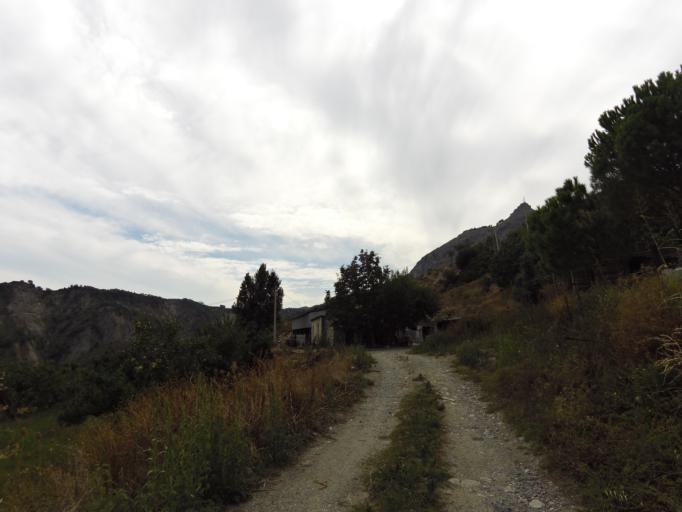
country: IT
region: Calabria
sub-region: Provincia di Reggio Calabria
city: Stilo
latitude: 38.4727
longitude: 16.4641
